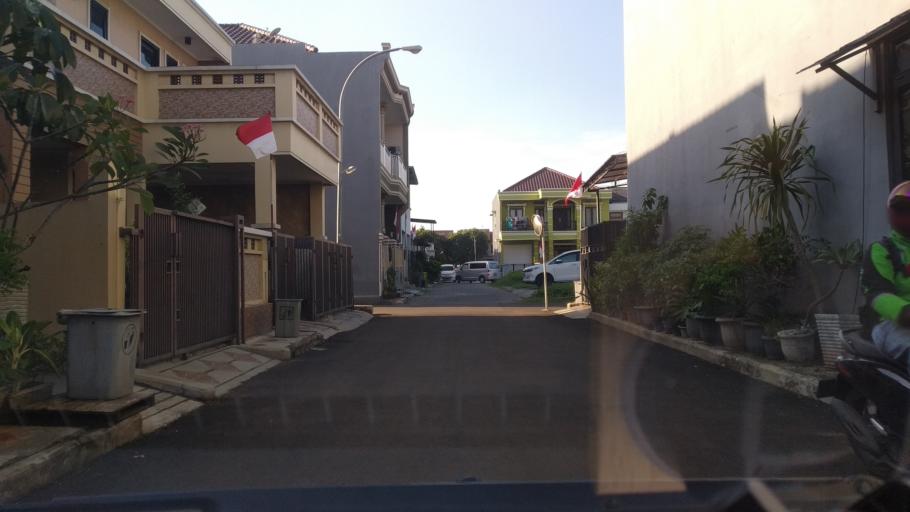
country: ID
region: Banten
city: South Tangerang
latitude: -6.2594
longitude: 106.7377
